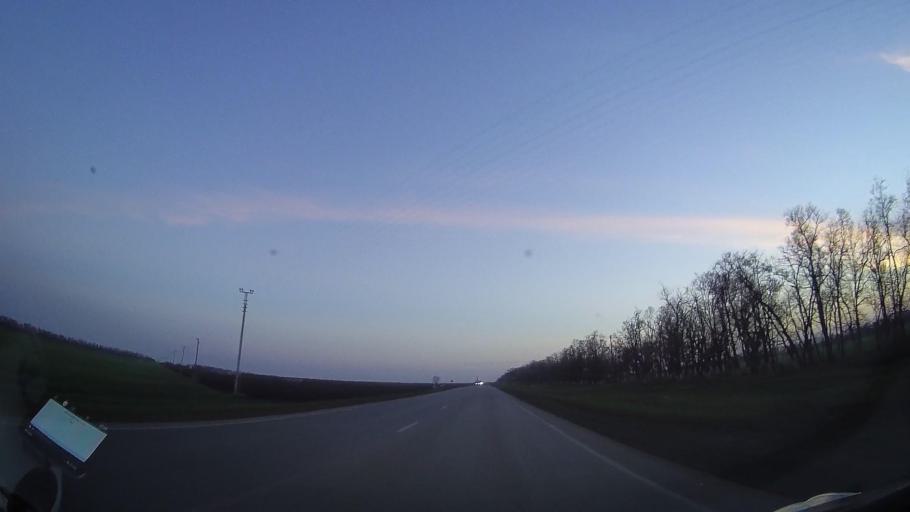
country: RU
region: Rostov
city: Zernograd
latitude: 46.8261
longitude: 40.2994
